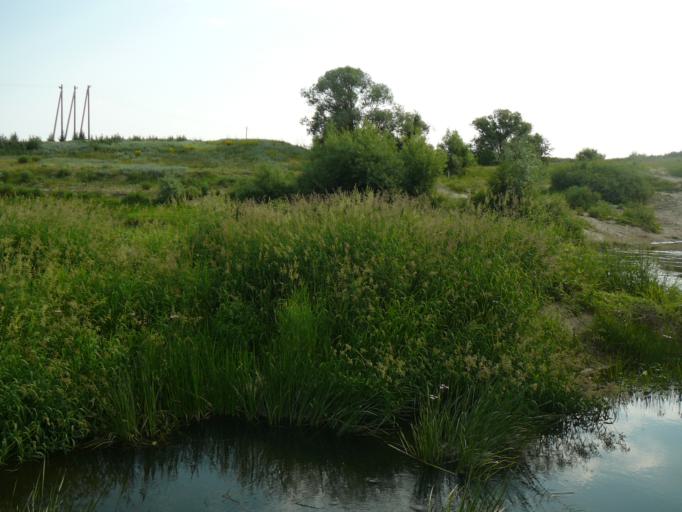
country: RU
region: Penza
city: Tamala
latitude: 52.2760
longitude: 43.3672
